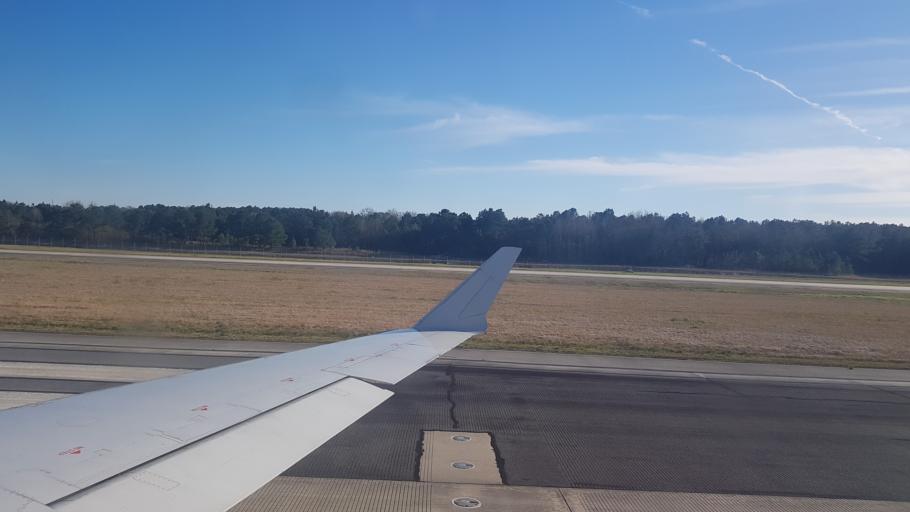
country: US
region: Georgia
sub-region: Chatham County
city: Pooler
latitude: 32.1288
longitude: -81.2172
